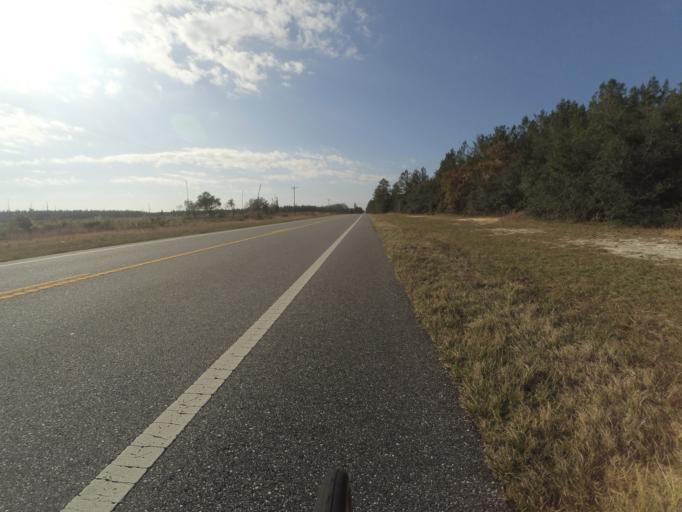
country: US
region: Florida
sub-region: Lake County
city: Astor
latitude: 29.1016
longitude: -81.6198
